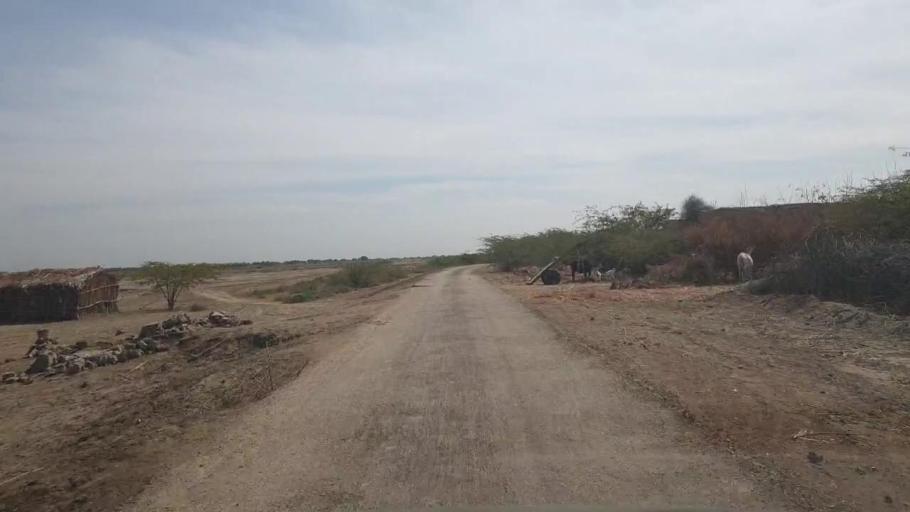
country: PK
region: Sindh
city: Kunri
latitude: 25.2692
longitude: 69.6015
